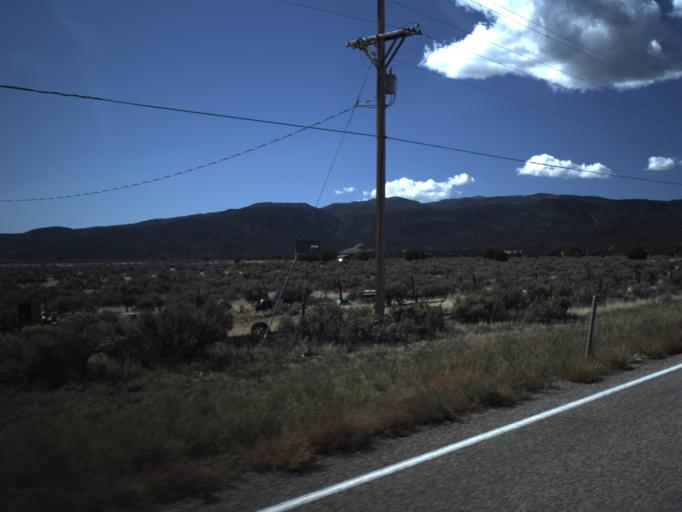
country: US
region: Utah
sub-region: Iron County
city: Cedar City
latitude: 37.6475
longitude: -113.2395
